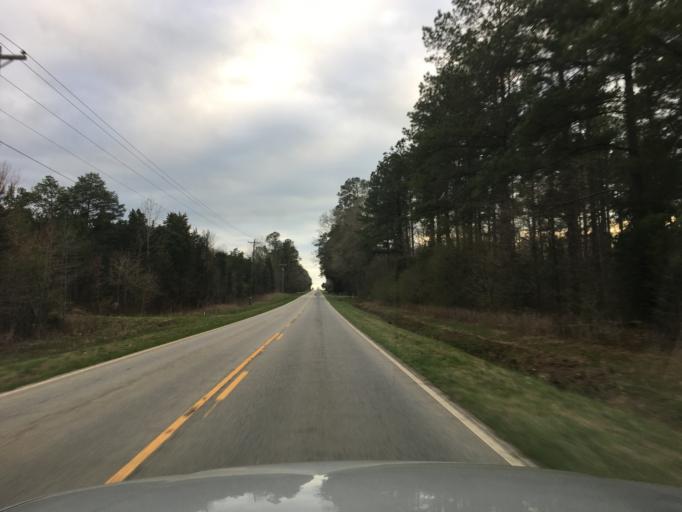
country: US
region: South Carolina
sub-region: Saluda County
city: Saluda
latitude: 33.9772
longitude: -81.7735
